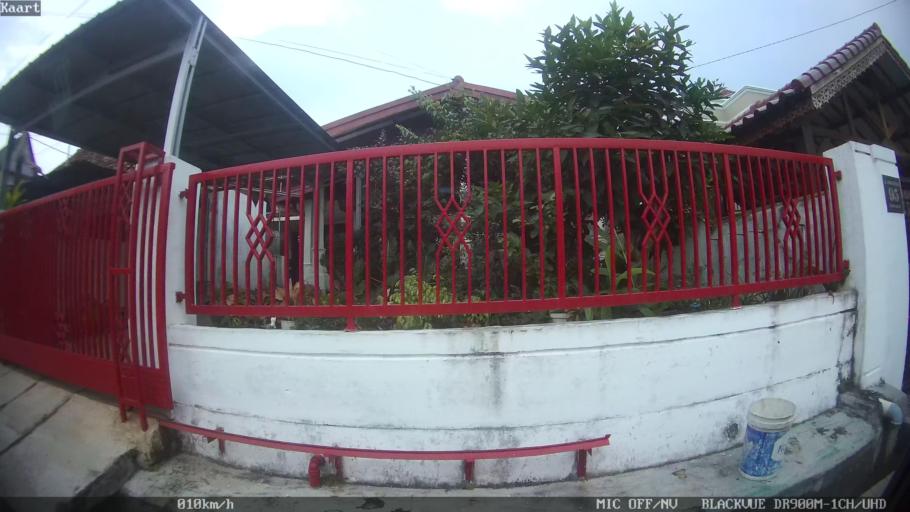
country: ID
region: Lampung
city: Bandarlampung
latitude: -5.4262
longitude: 105.2577
